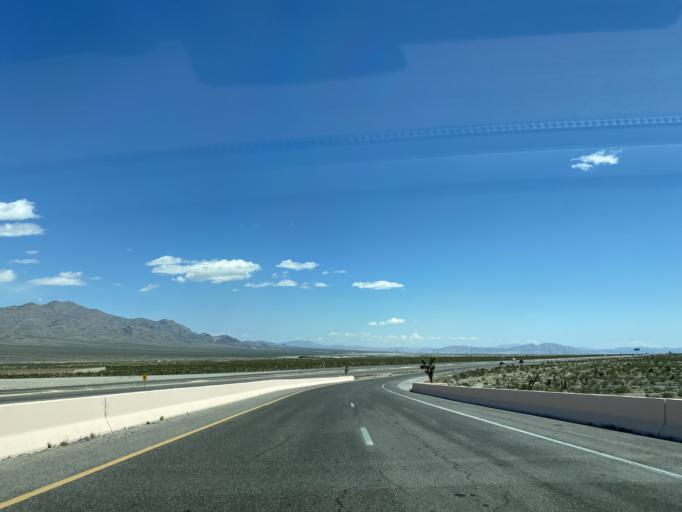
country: US
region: Nevada
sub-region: Clark County
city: Summerlin South
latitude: 36.3607
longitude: -115.3517
